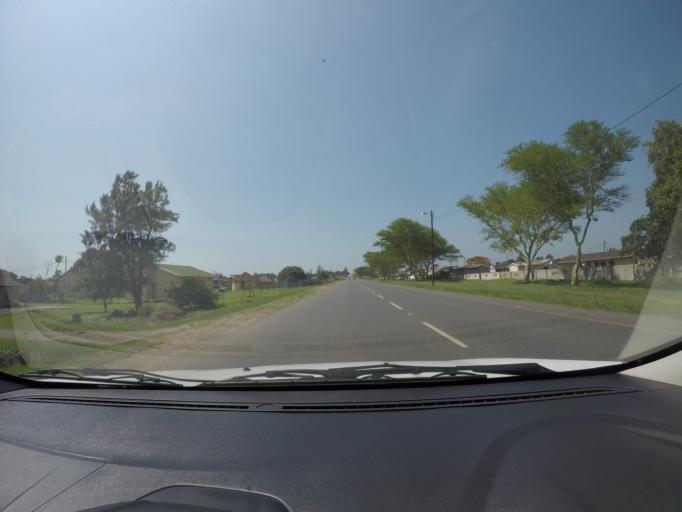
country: ZA
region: KwaZulu-Natal
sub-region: uThungulu District Municipality
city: eSikhawini
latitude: -28.8603
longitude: 31.9243
